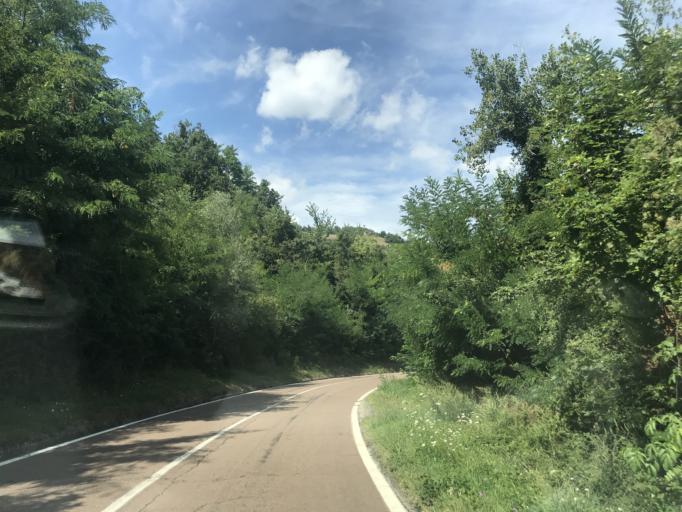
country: IT
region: Emilia-Romagna
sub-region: Provincia di Bologna
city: Grizzana
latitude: 44.2574
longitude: 11.1610
